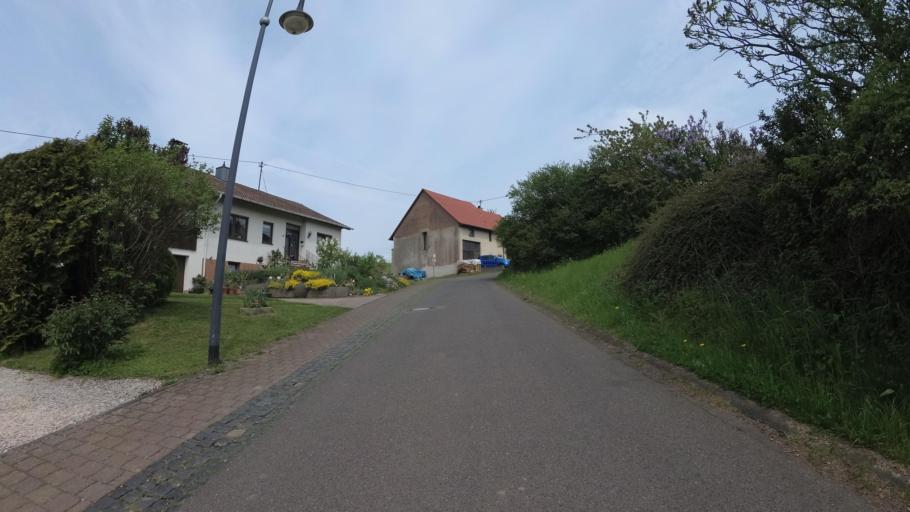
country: DE
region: Rheinland-Pfalz
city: Eckersweiler
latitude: 49.5611
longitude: 7.2964
